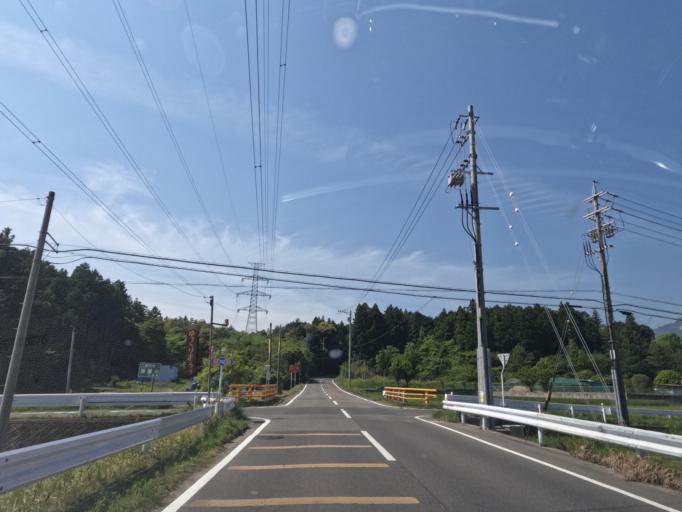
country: JP
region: Mie
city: Komono
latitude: 35.0328
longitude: 136.4917
